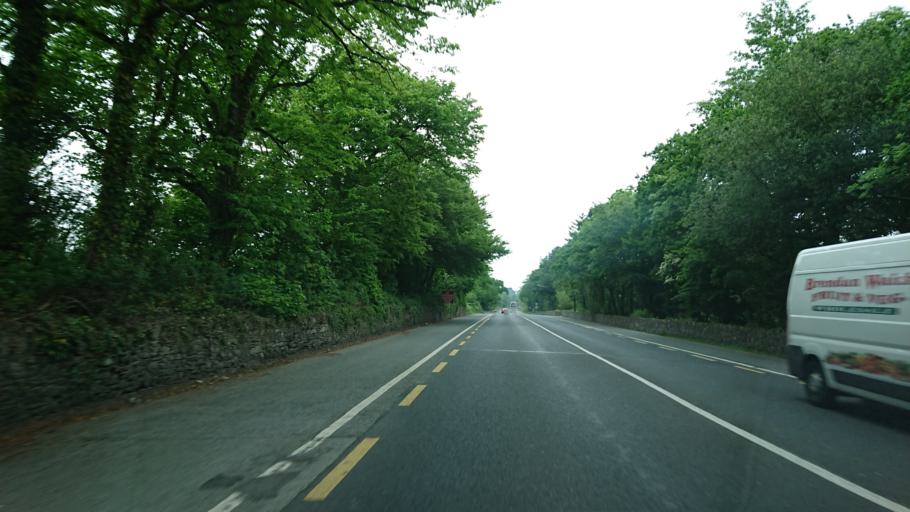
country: IE
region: Munster
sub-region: Waterford
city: Waterford
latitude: 52.2175
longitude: -7.1264
